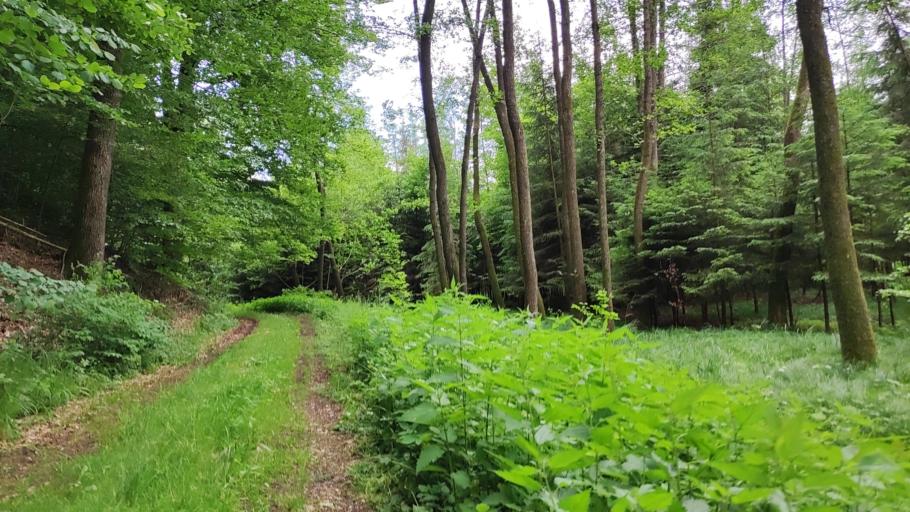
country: DE
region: Bavaria
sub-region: Swabia
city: Landensberg
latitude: 48.4309
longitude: 10.5076
